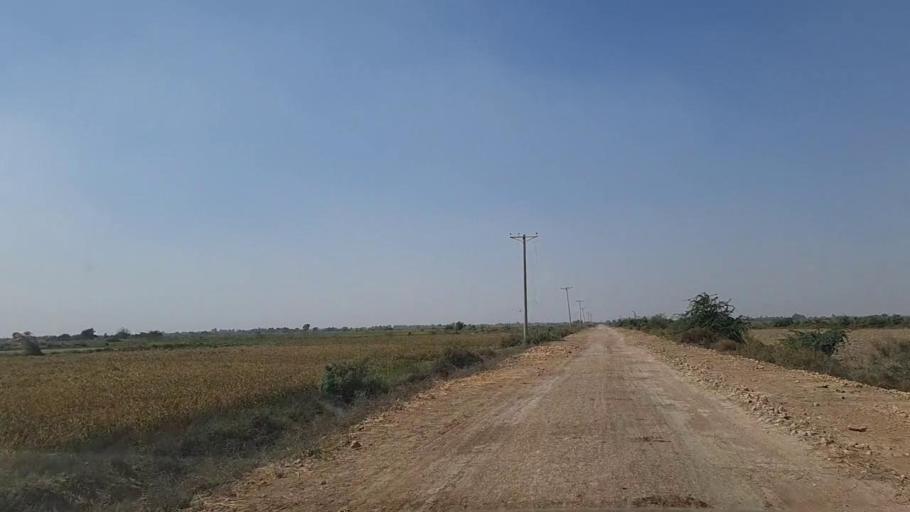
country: PK
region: Sindh
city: Daro Mehar
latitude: 24.8329
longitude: 68.1722
